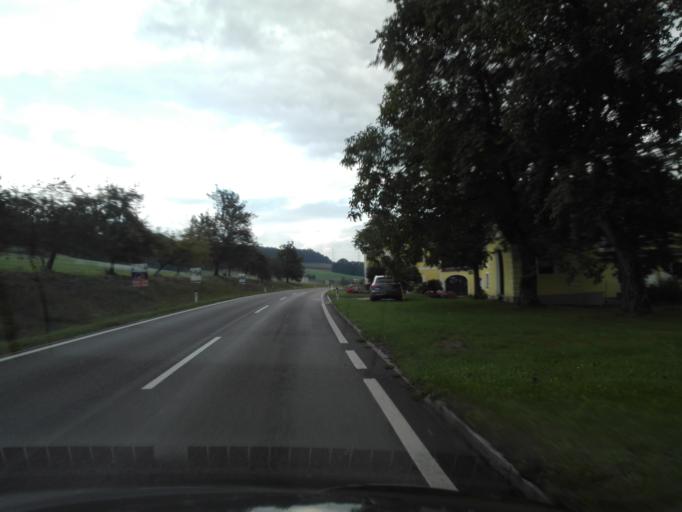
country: DE
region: Bavaria
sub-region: Lower Bavaria
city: Bad Fussing
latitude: 48.2386
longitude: 13.3531
